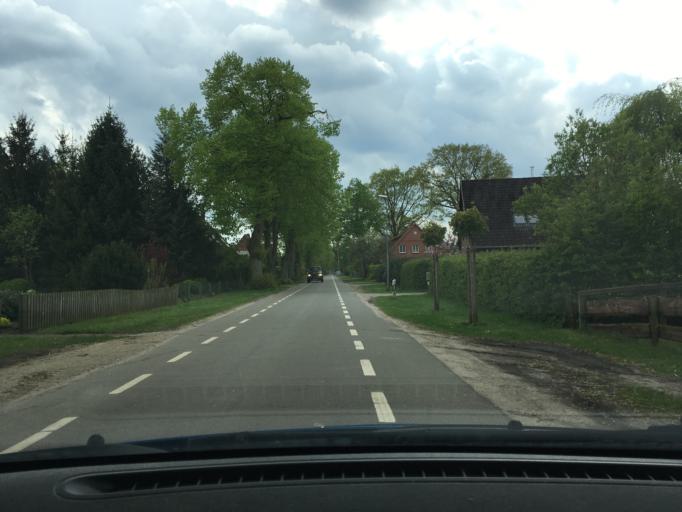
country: DE
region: Lower Saxony
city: Radbruch
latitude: 53.3044
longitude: 10.2750
